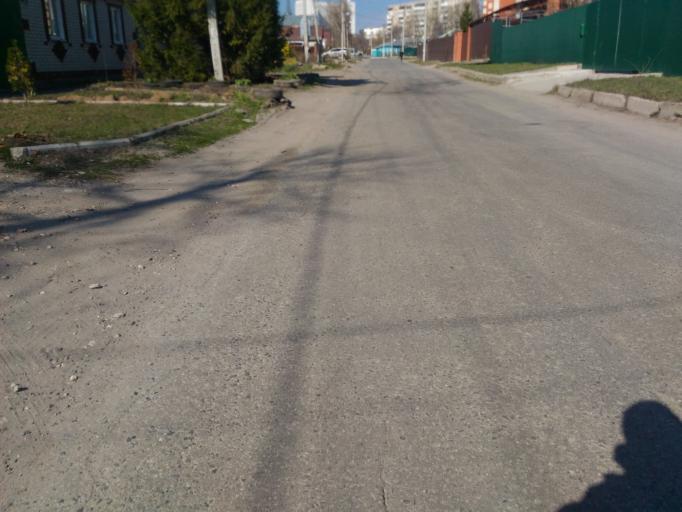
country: RU
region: Ulyanovsk
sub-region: Ulyanovskiy Rayon
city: Ulyanovsk
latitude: 54.3283
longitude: 48.3822
